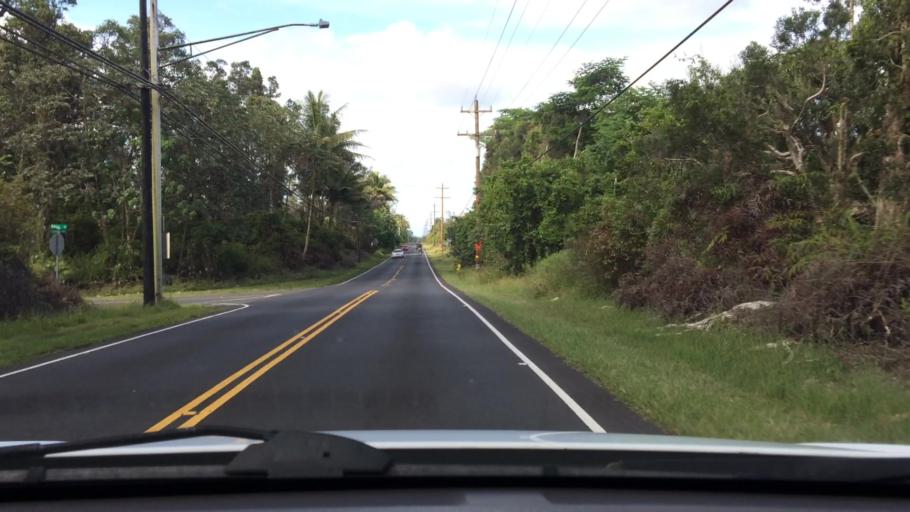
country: US
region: Hawaii
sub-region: Hawaii County
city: Nanawale Estates
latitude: 19.5131
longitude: -154.9416
